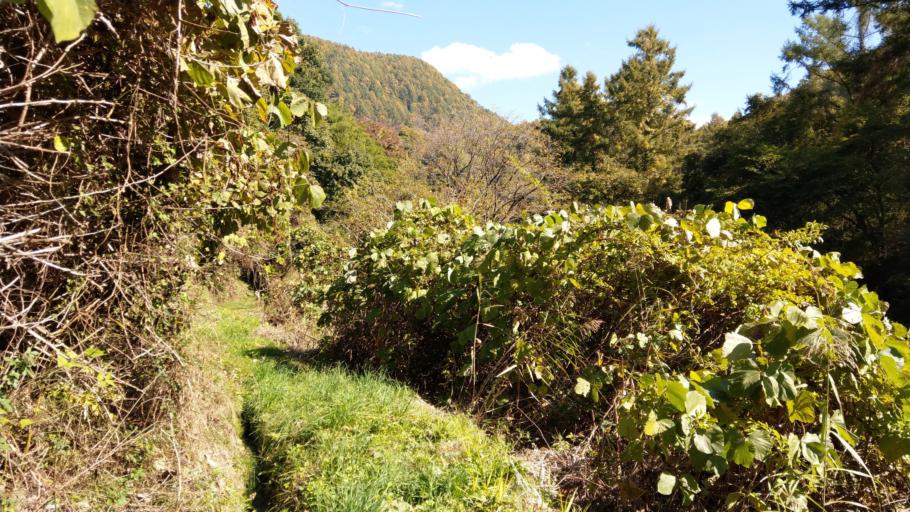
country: JP
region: Nagano
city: Komoro
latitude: 36.3726
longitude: 138.4142
